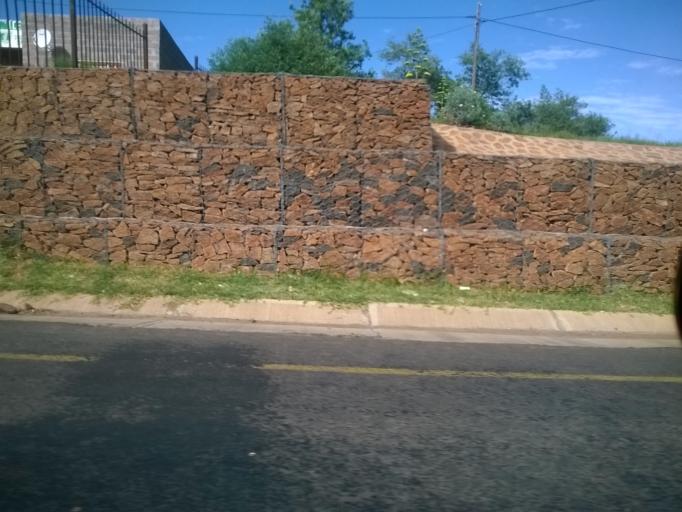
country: LS
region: Berea
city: Teyateyaneng
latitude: -29.1032
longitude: 27.9609
